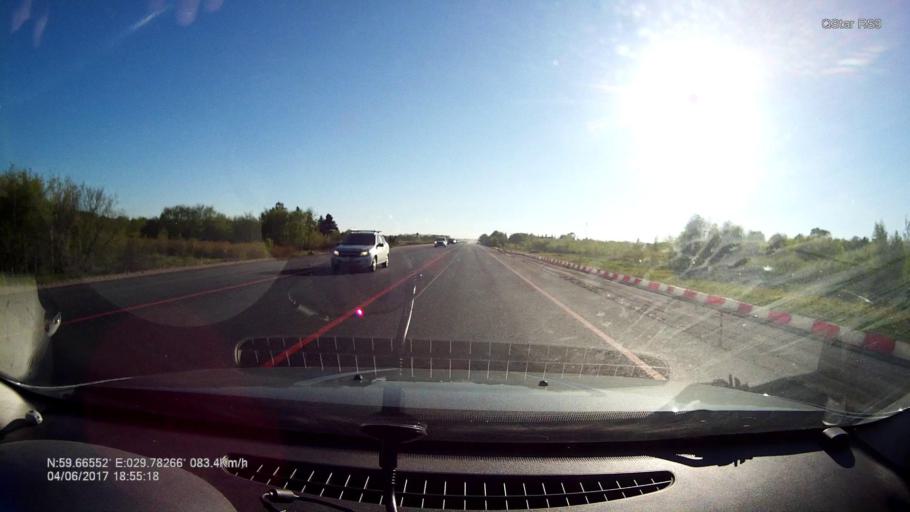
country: RU
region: Leningrad
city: Kipen'
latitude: 59.6655
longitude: 29.7826
